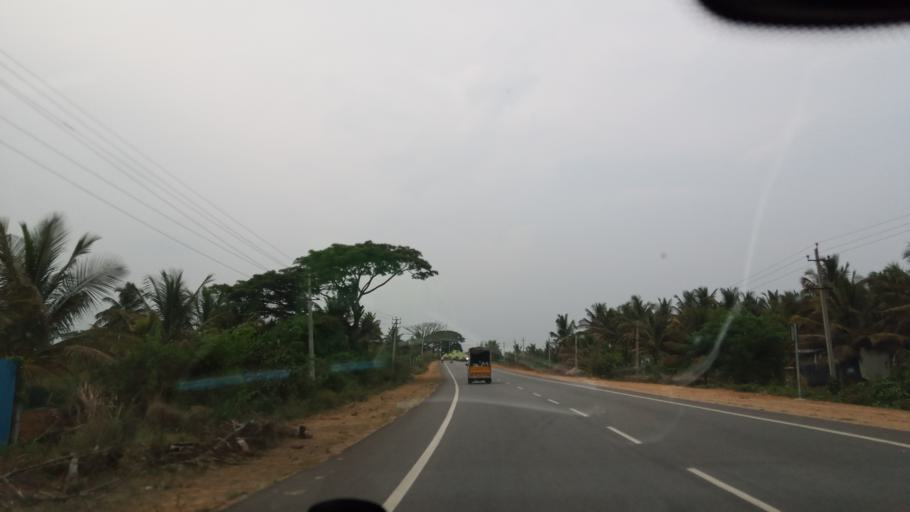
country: IN
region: Karnataka
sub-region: Mandya
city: Nagamangala
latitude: 12.7303
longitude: 76.7174
